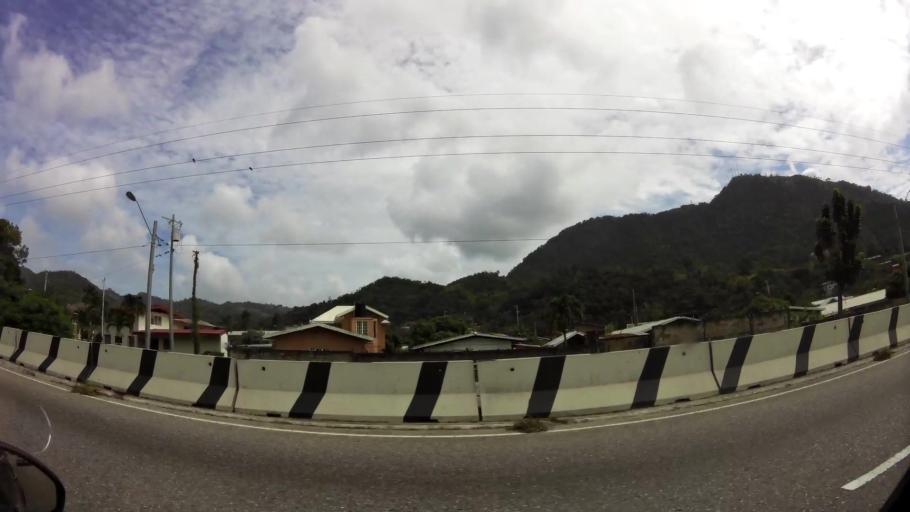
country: TT
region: Diego Martin
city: Petit Valley
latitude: 10.7027
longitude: -61.5533
